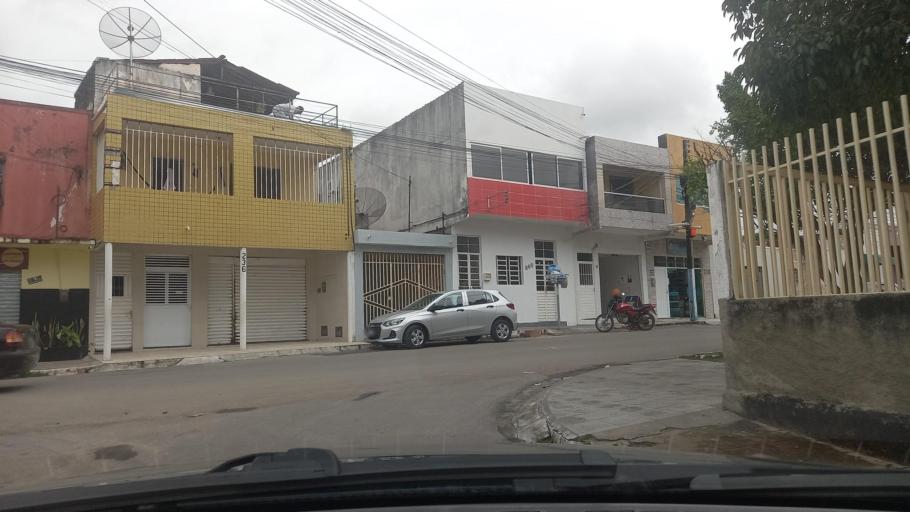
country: BR
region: Alagoas
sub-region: Delmiro Gouveia
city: Delmiro Gouveia
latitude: -9.3867
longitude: -37.9981
